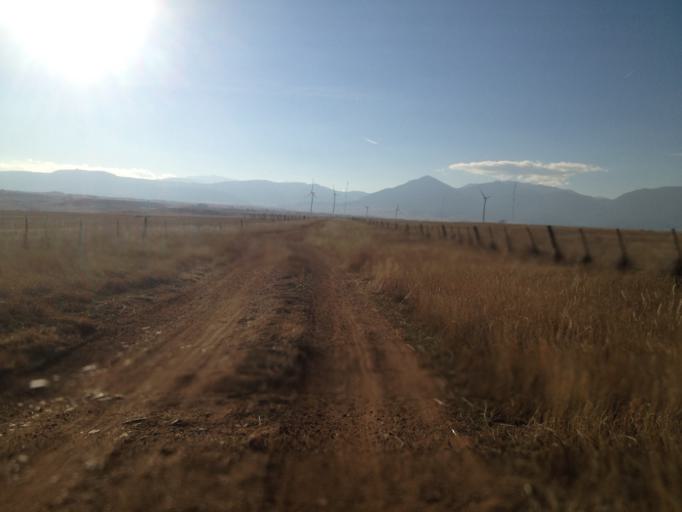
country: US
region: Colorado
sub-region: Boulder County
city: Superior
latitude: 39.9165
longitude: -105.2013
